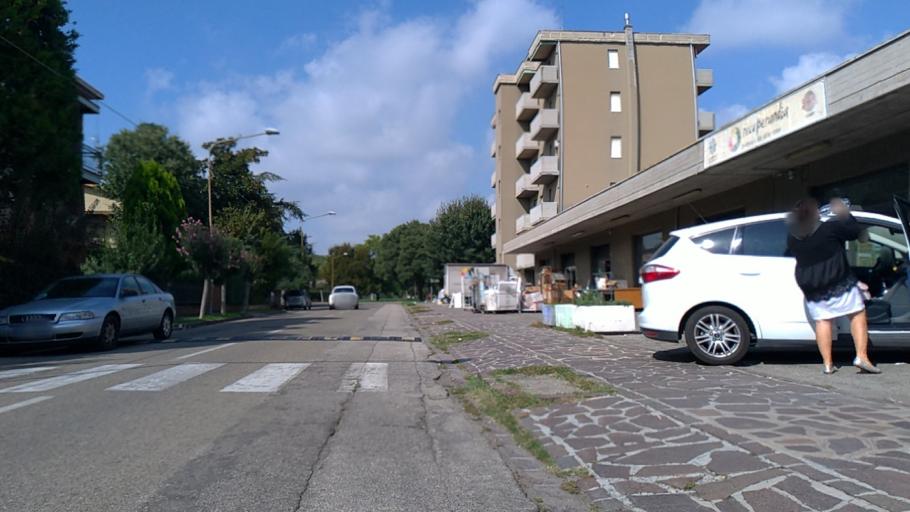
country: IT
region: Emilia-Romagna
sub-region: Provincia di Modena
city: Carpi Centro
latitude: 44.7696
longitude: 10.8729
